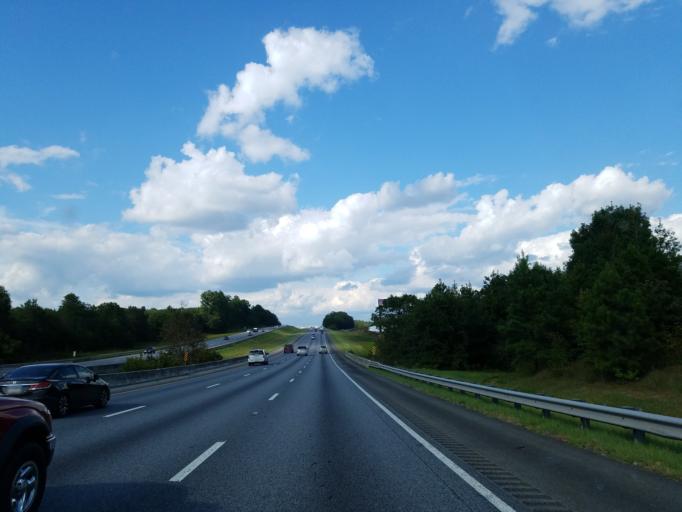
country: US
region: South Carolina
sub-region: Anderson County
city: Piedmont
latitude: 34.7341
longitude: -82.4878
